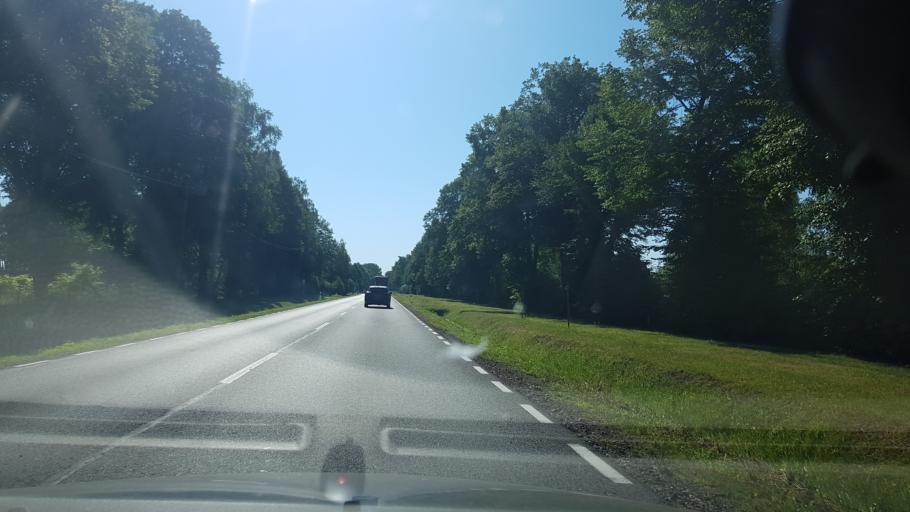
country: PL
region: Masovian Voivodeship
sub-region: Powiat wegrowski
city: Lochow
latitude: 52.5518
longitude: 21.6149
